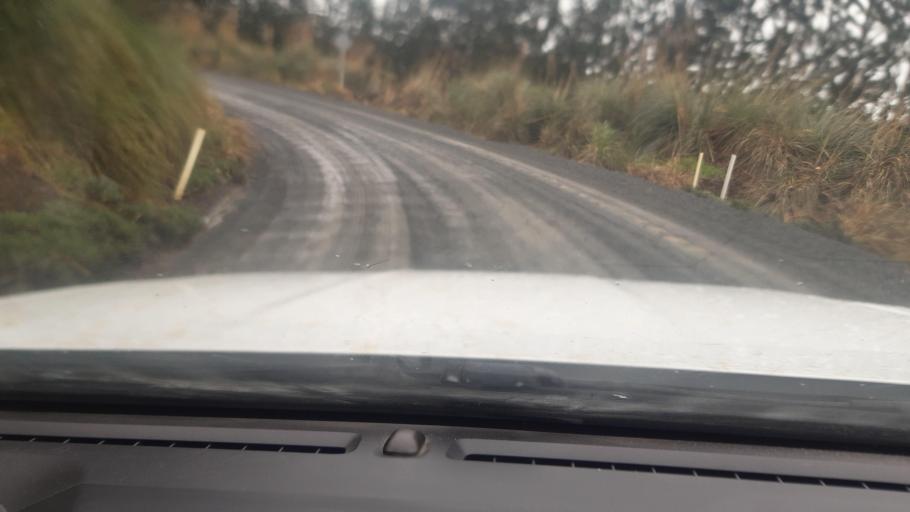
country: NZ
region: Northland
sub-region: Far North District
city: Kaitaia
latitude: -34.9774
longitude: 173.2021
